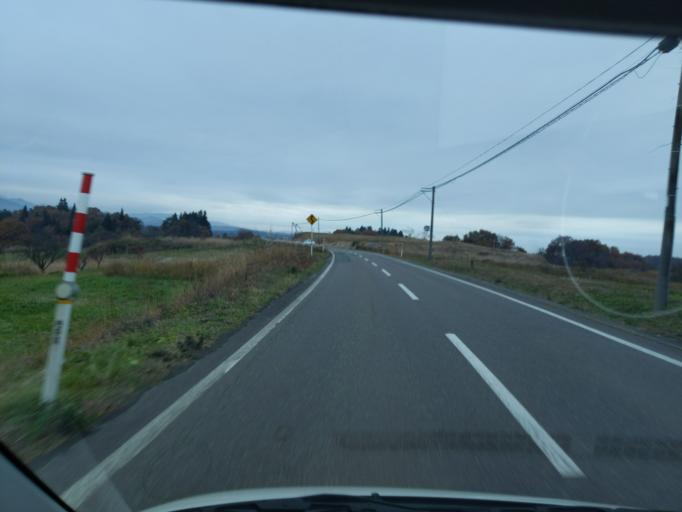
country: JP
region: Iwate
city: Kitakami
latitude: 39.2364
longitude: 141.2378
